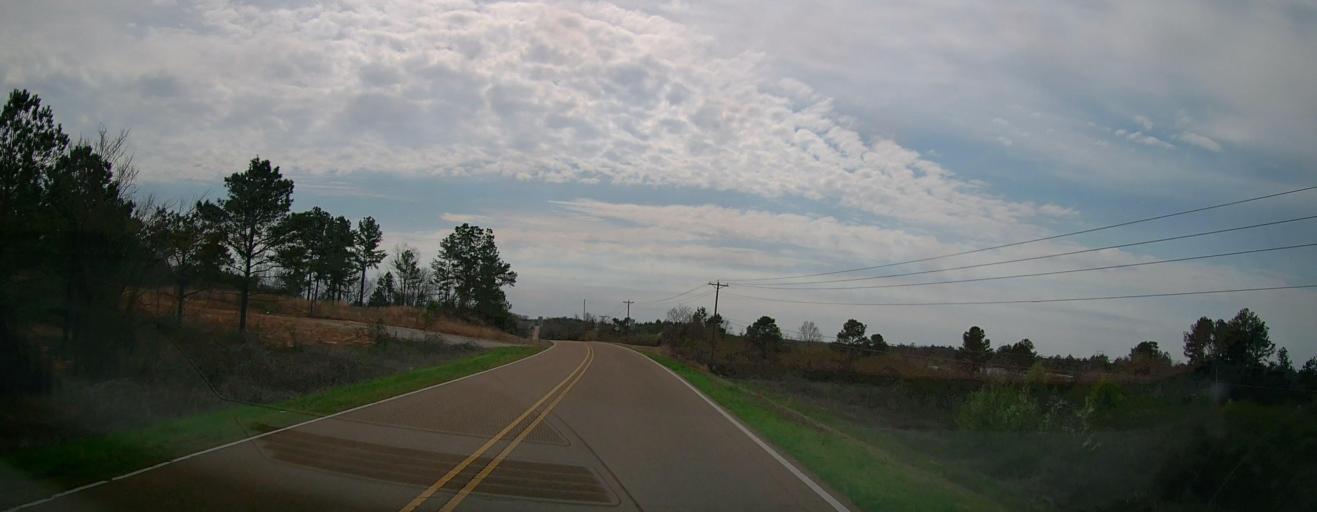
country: US
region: Mississippi
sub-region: Marshall County
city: Holly Springs
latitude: 34.7516
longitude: -89.4297
